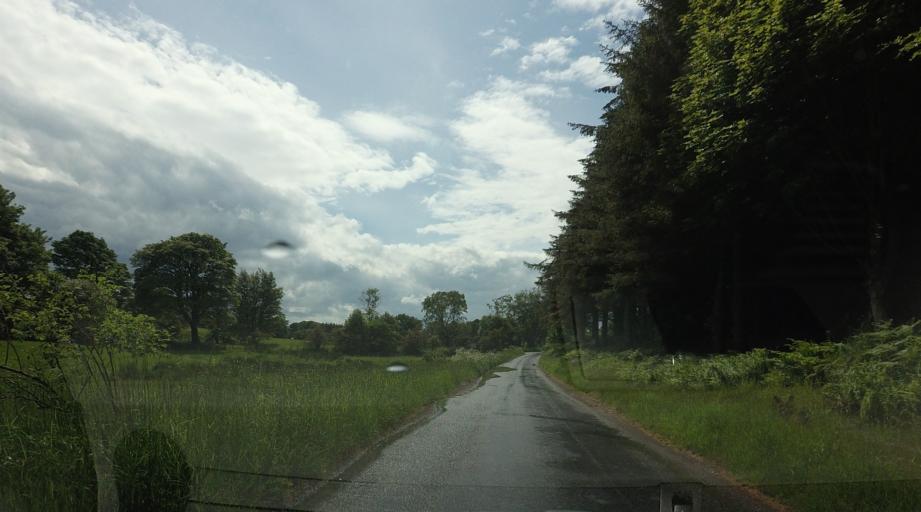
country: GB
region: Scotland
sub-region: Fife
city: Ballingry
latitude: 56.1584
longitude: -3.3541
